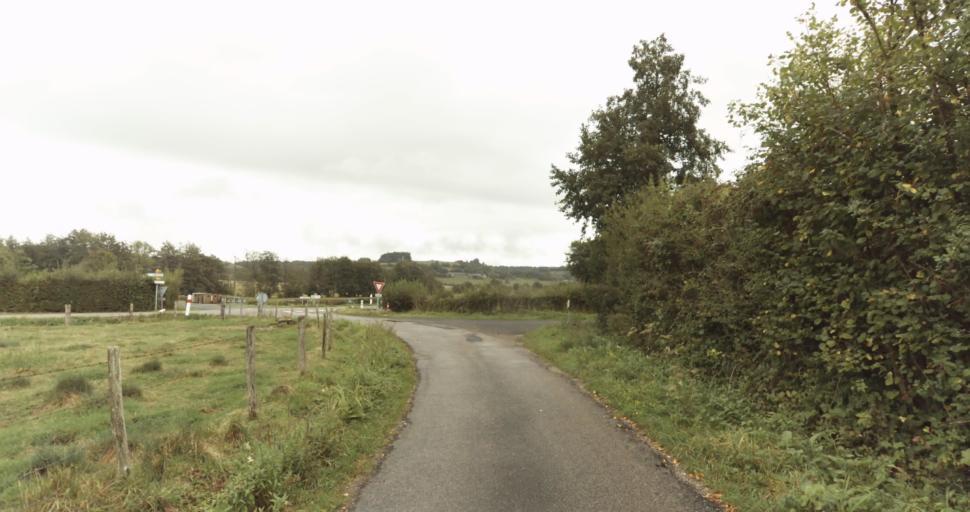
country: FR
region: Lower Normandy
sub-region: Departement de l'Orne
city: Vimoutiers
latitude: 48.8763
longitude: 0.2194
